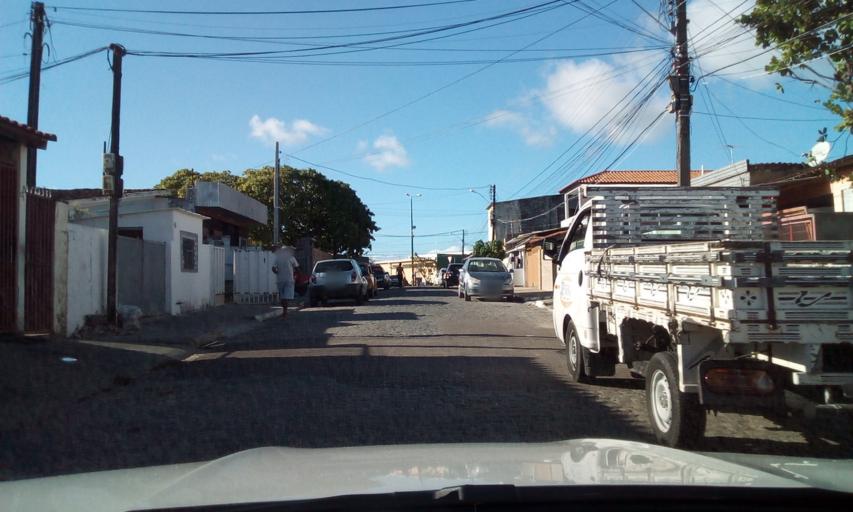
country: BR
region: Paraiba
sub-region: Joao Pessoa
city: Joao Pessoa
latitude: -7.1080
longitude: -34.8599
